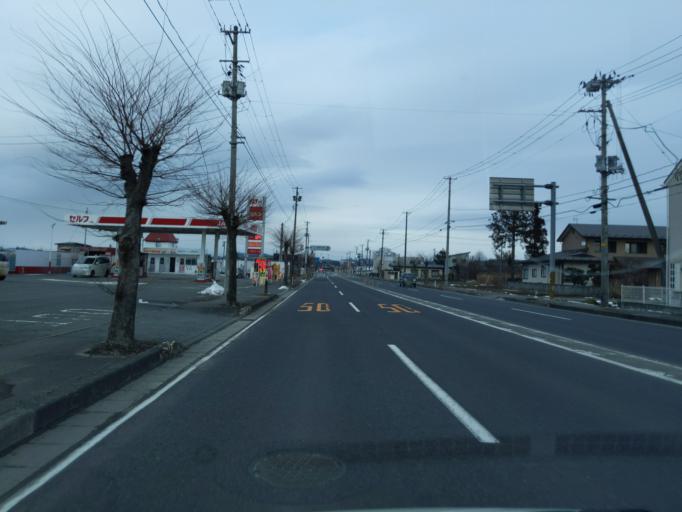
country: JP
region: Iwate
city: Mizusawa
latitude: 39.1736
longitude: 141.1582
